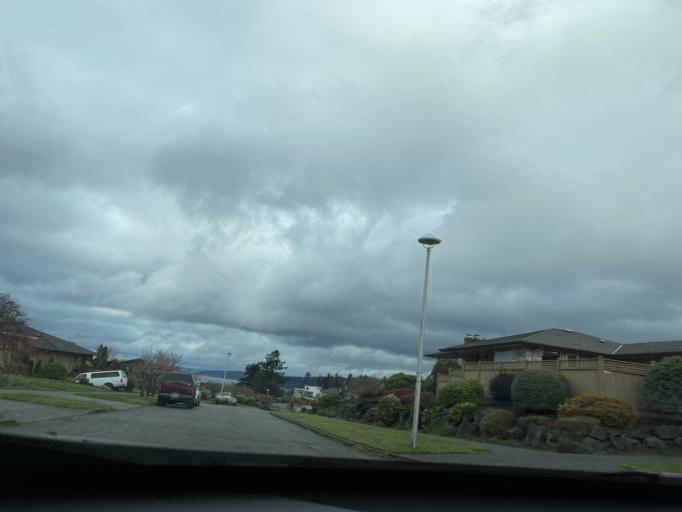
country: US
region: Washington
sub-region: King County
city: Shoreline
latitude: 47.6962
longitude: -122.3856
